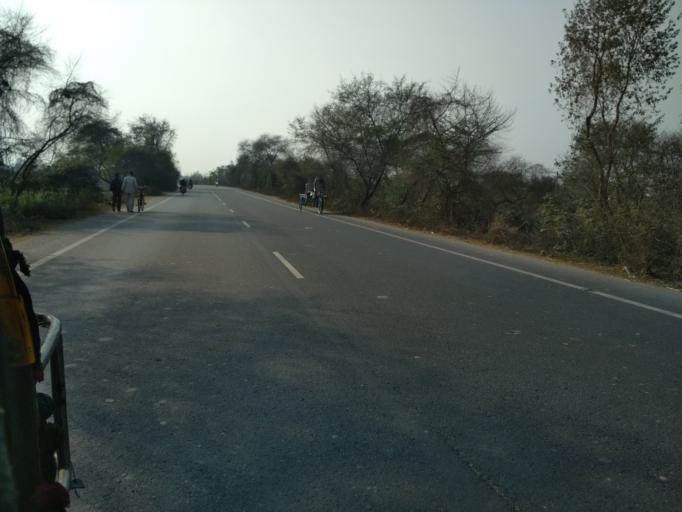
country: IN
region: Bihar
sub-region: Khagaria
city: Khagaria
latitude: 25.5079
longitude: 86.5466
